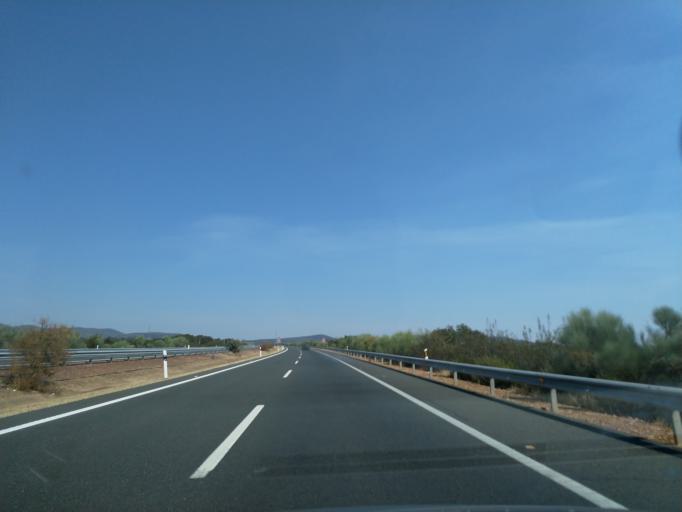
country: ES
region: Extremadura
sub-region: Provincia de Badajoz
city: Carmonita
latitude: 39.1052
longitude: -6.2824
